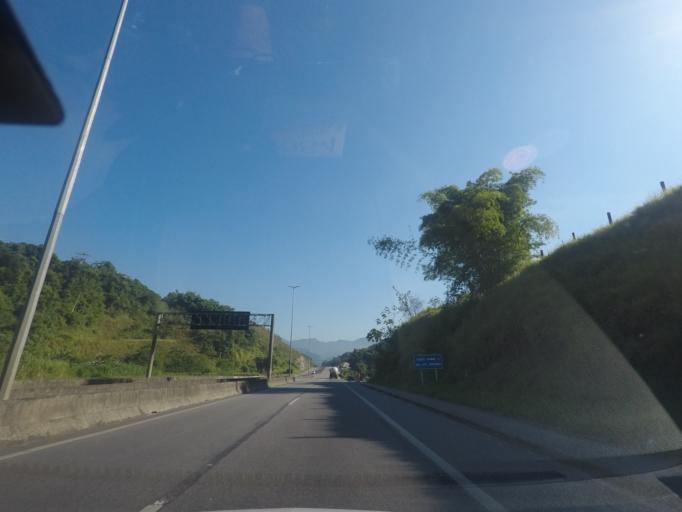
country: BR
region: Rio de Janeiro
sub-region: Petropolis
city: Petropolis
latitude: -22.6062
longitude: -43.2853
